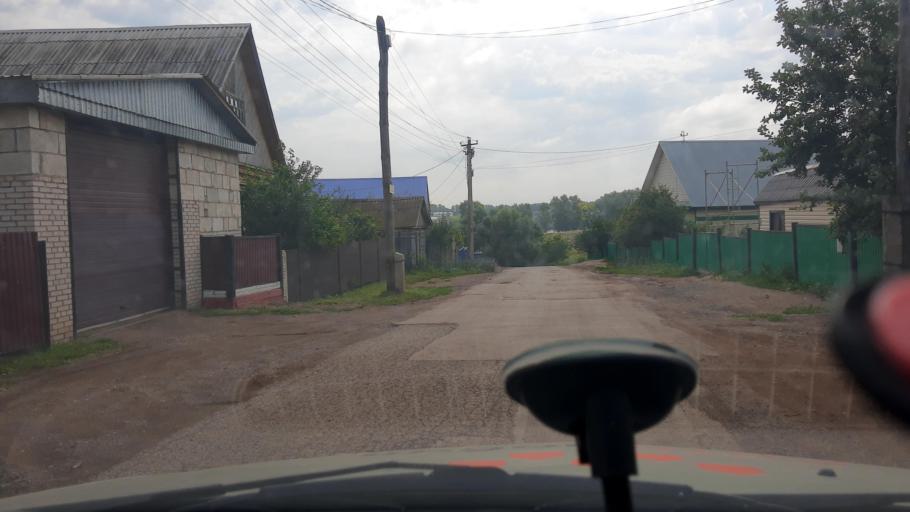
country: RU
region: Bashkortostan
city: Chishmy
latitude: 54.6057
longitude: 55.3970
